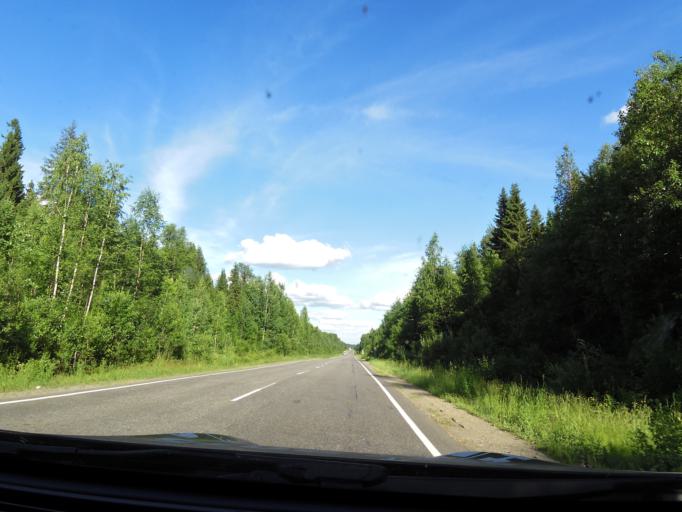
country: RU
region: Kirov
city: Omutninsk
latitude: 58.7607
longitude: 52.0095
